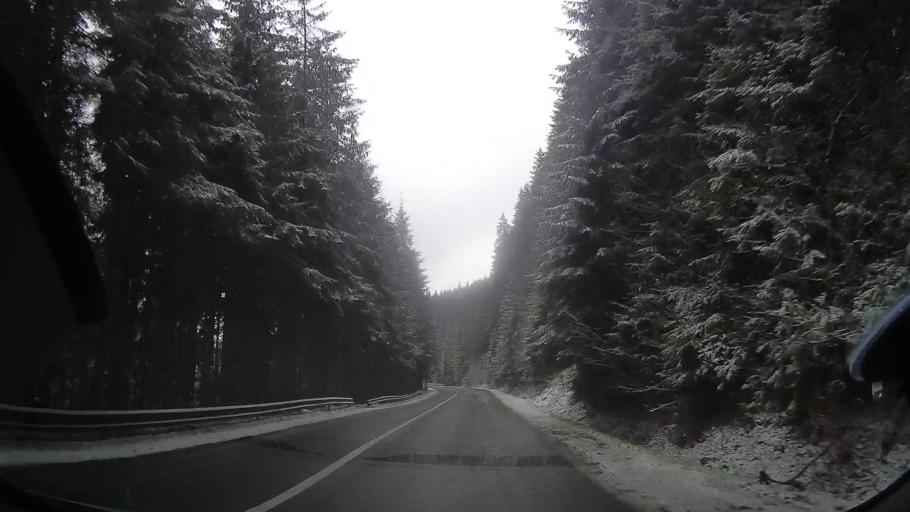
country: RO
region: Cluj
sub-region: Comuna Belis
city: Belis
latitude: 46.6498
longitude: 23.0514
